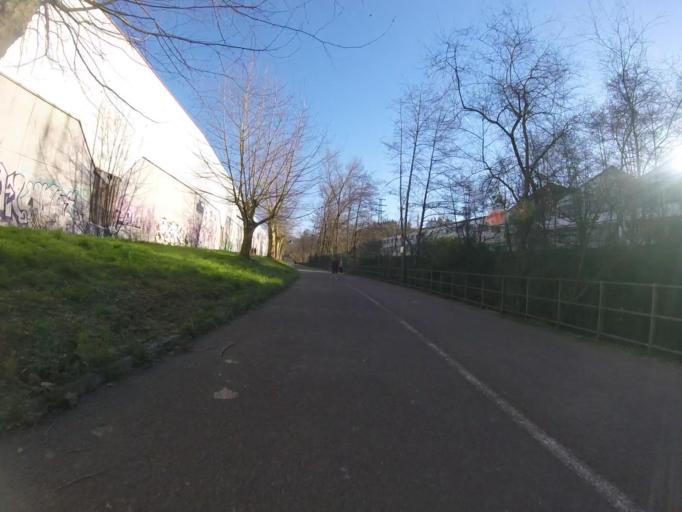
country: ES
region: Basque Country
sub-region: Provincia de Guipuzcoa
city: Errenteria
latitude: 43.3048
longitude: -1.8860
